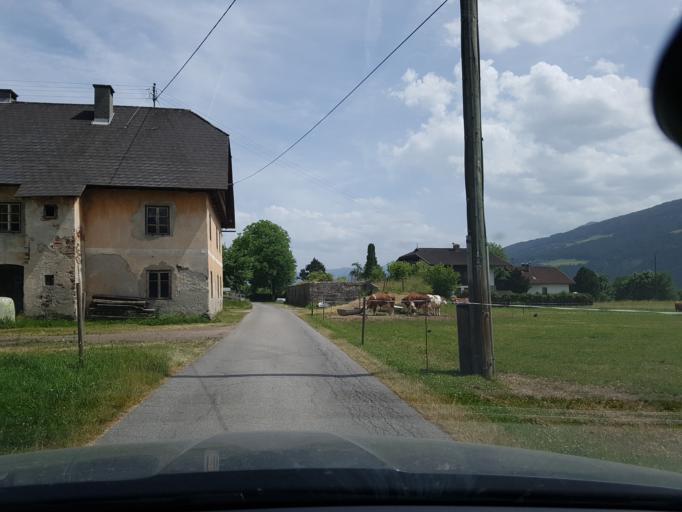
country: AT
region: Carinthia
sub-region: Politischer Bezirk Spittal an der Drau
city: Millstatt
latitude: 46.7788
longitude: 13.5491
